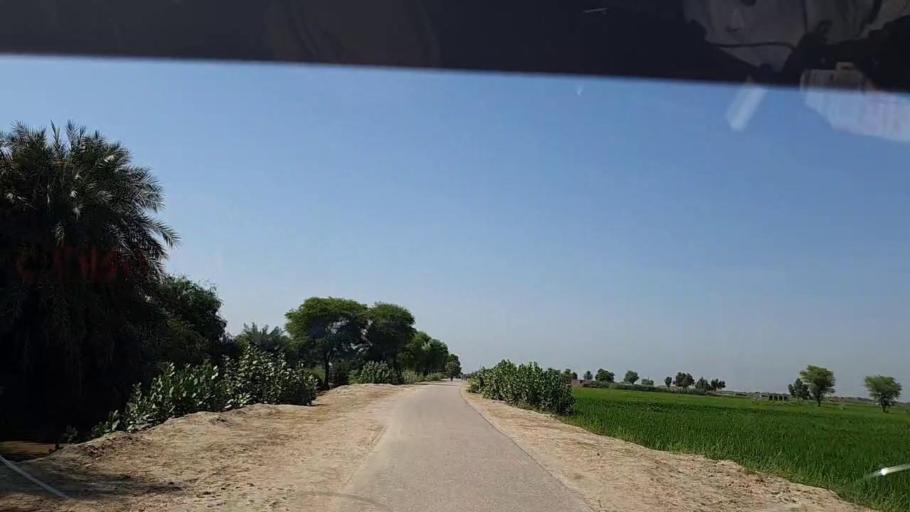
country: PK
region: Sindh
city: Kandhkot
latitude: 28.3060
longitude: 69.1104
